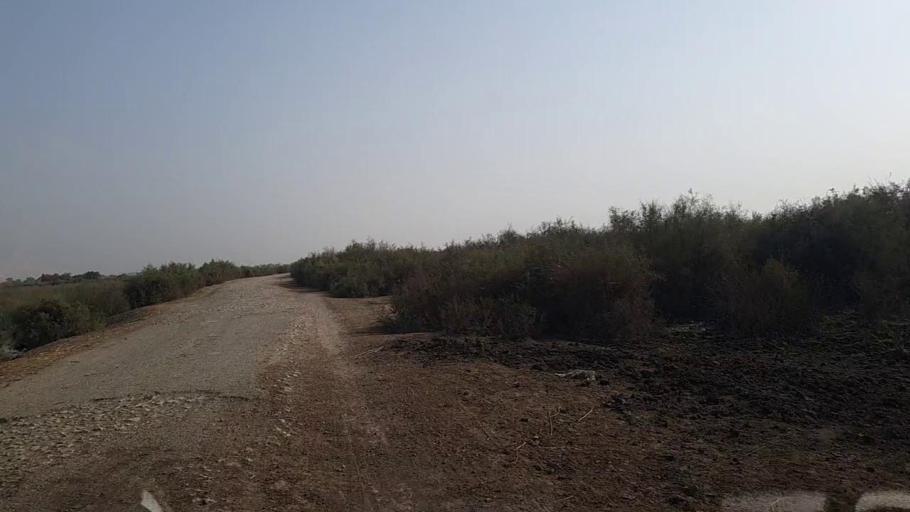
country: PK
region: Sindh
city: Kandhkot
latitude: 28.2955
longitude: 69.2526
